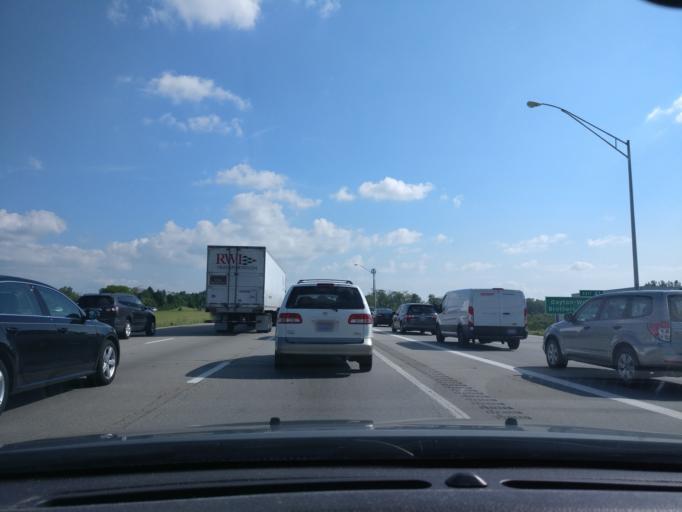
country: US
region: Ohio
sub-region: Warren County
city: Five Points
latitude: 39.6119
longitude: -84.2338
